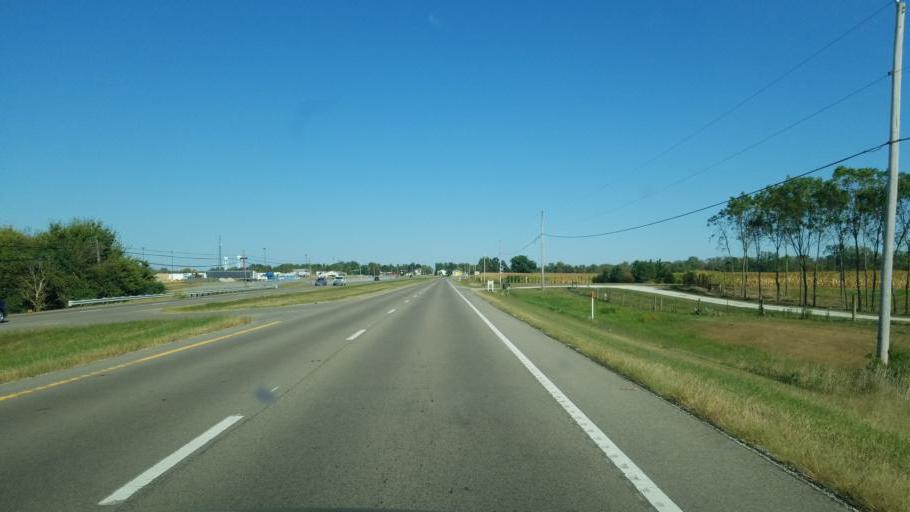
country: US
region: Ohio
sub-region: Clark County
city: Lisbon
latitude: 39.9269
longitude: -83.6283
